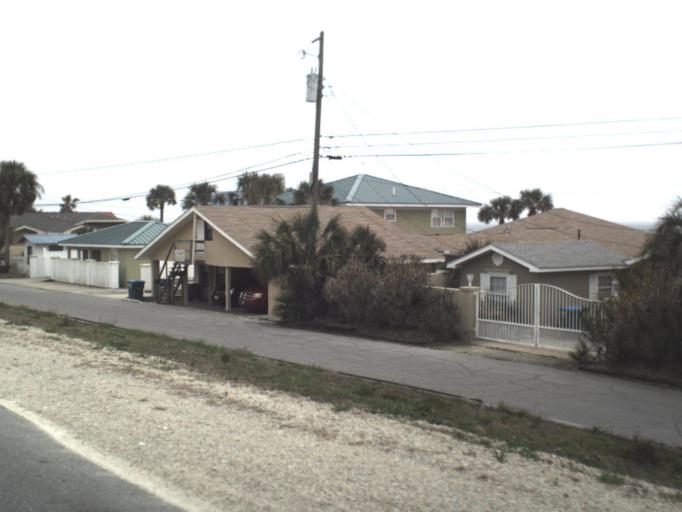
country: US
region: Florida
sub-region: Bay County
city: Panama City Beach
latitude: 30.1967
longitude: -85.8417
